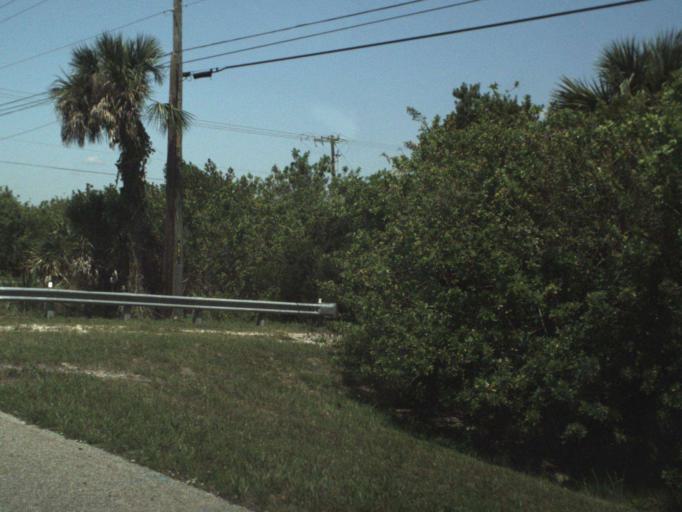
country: US
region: Florida
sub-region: Brevard County
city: Merritt Island
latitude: 28.4757
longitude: -80.7005
